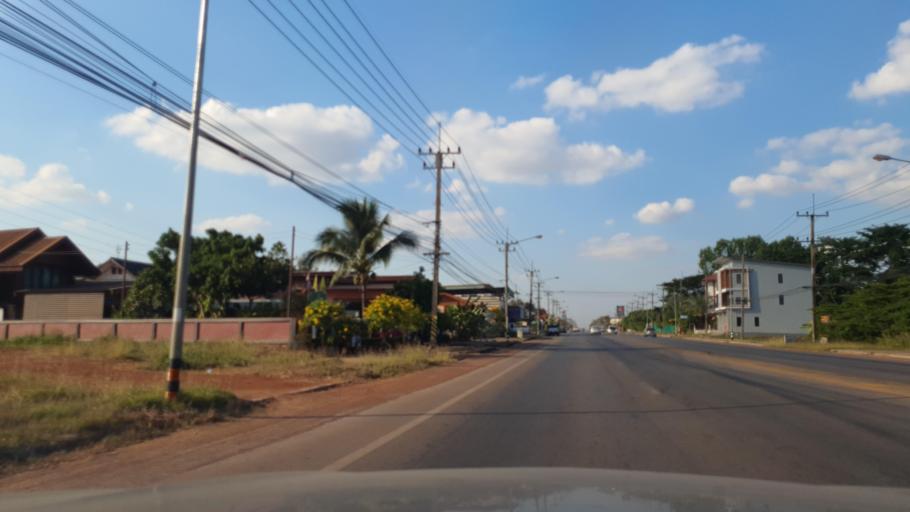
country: TH
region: Sakon Nakhon
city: Sakon Nakhon
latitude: 17.1717
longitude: 104.0986
